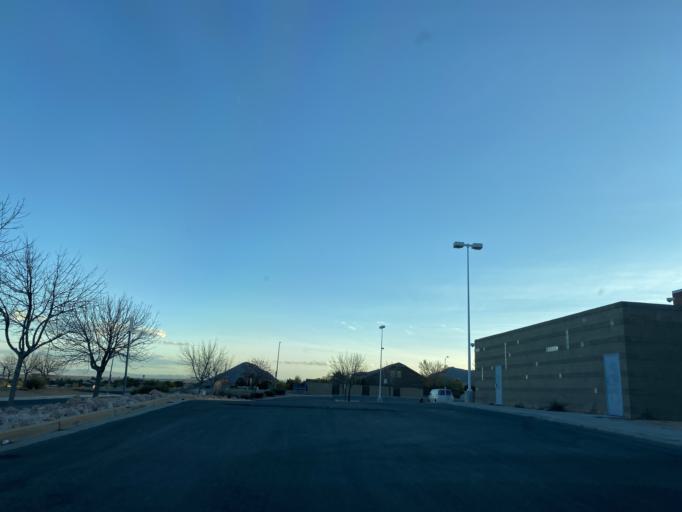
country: US
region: Nevada
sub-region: Clark County
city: Summerlin South
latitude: 36.2783
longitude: -115.3213
